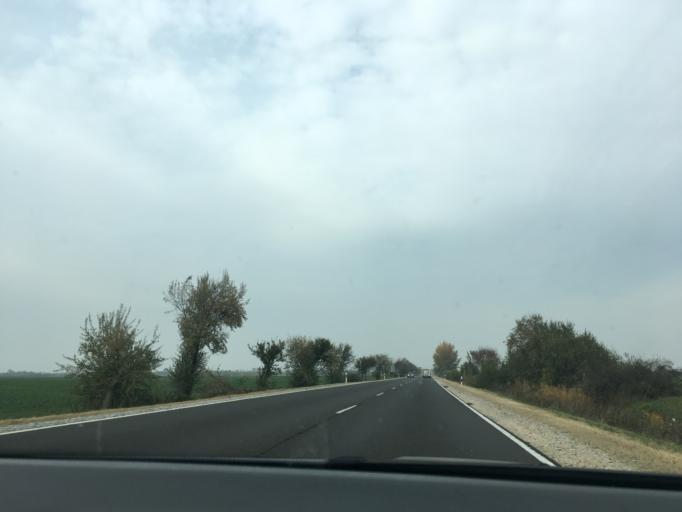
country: HU
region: Jasz-Nagykun-Szolnok
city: Toszeg
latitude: 47.1661
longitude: 20.1047
